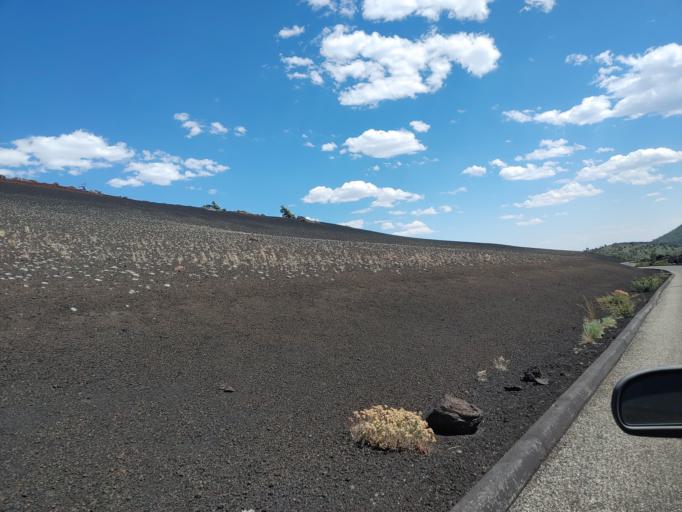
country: US
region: Idaho
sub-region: Butte County
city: Arco
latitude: 43.4424
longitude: -113.5545
